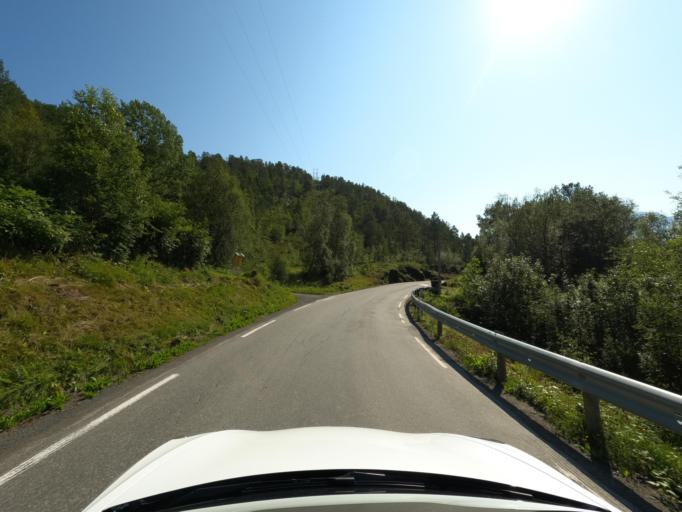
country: NO
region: Nordland
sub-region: Narvik
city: Narvik
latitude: 68.3652
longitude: 17.2619
